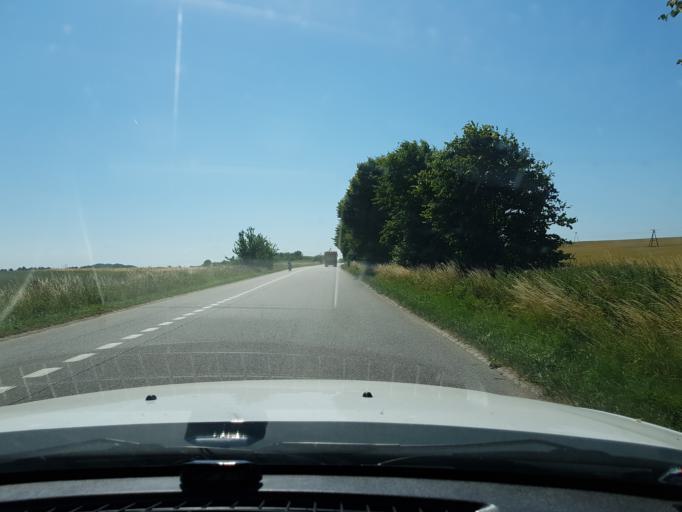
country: PL
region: West Pomeranian Voivodeship
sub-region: Powiat koszalinski
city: Mielno
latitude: 54.2098
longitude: 16.0685
